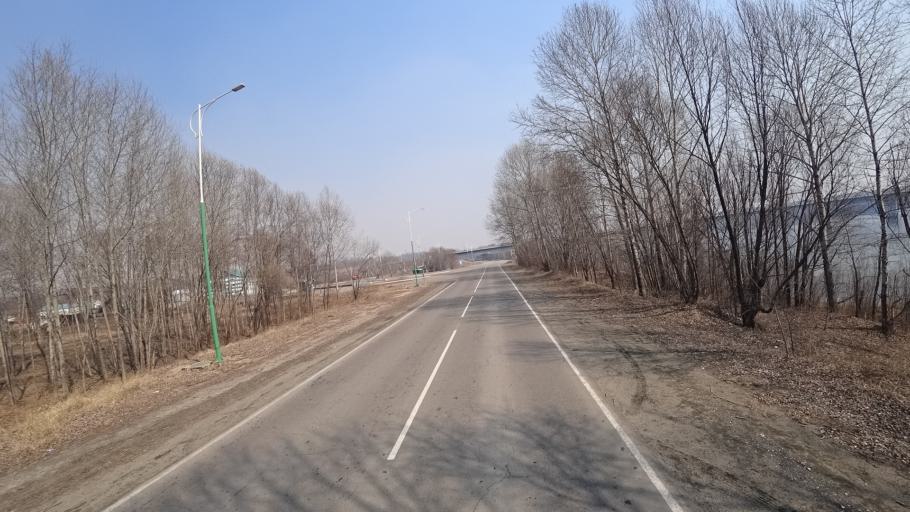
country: RU
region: Amur
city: Novobureyskiy
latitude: 49.7848
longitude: 129.9351
